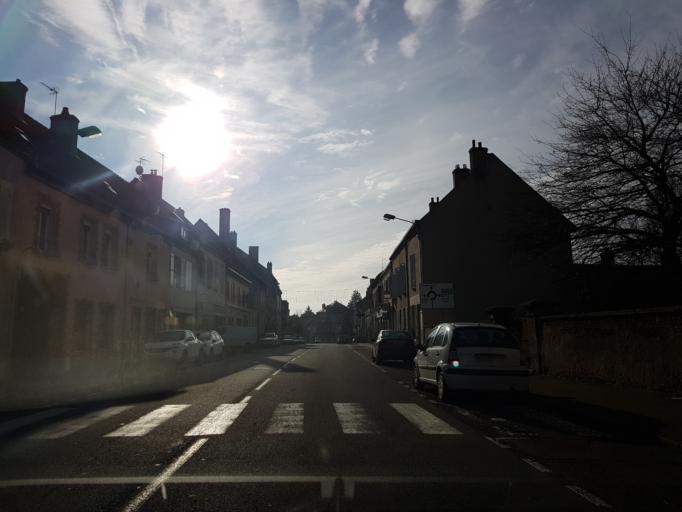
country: FR
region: Bourgogne
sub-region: Departement de Saone-et-Loire
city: Bourbon-Lancy
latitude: 46.6219
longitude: 3.7731
